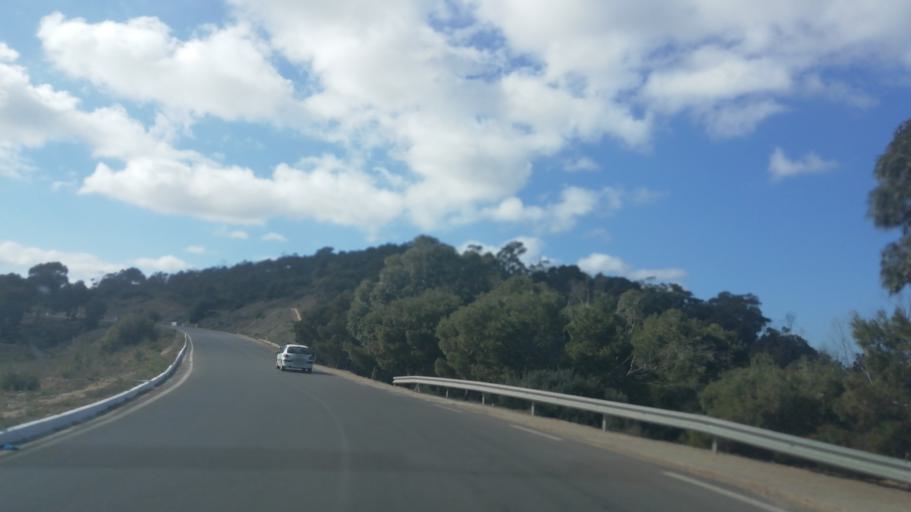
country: DZ
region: Relizane
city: Relizane
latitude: 36.0926
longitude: 0.4678
